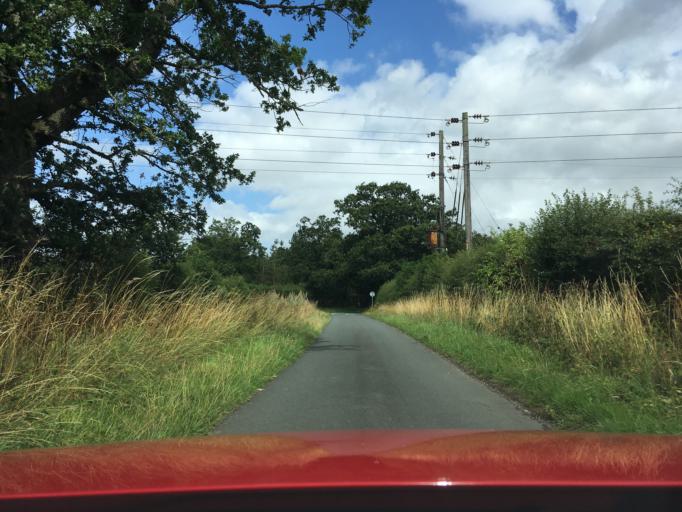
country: GB
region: England
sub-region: West Berkshire
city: Welford
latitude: 51.4237
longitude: -1.4015
